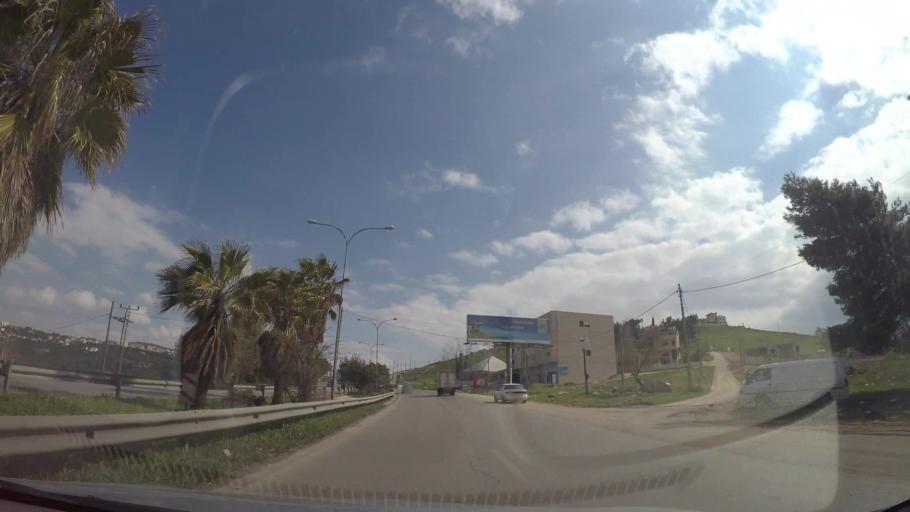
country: JO
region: Balqa
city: As Salt
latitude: 32.0354
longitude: 35.7912
